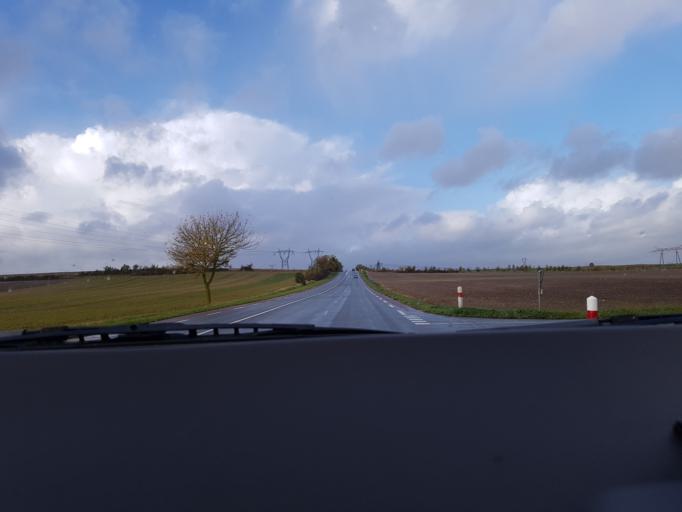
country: FR
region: Poitou-Charentes
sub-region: Departement de la Charente-Maritime
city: Les Gonds
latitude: 45.6685
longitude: -0.5988
